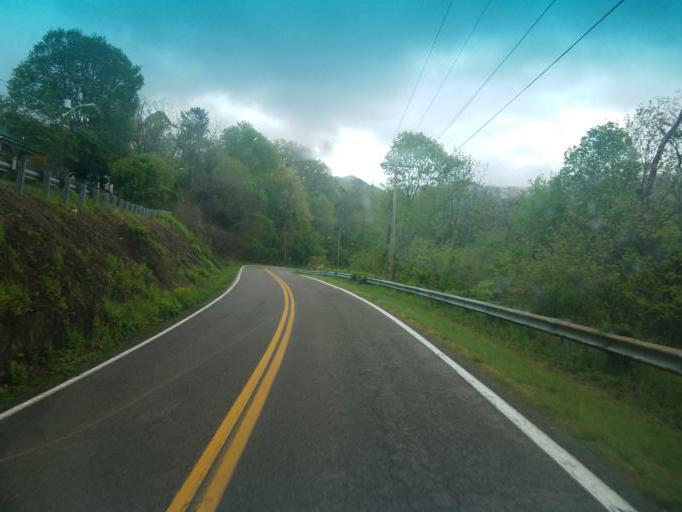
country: US
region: Virginia
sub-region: Washington County
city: Emory
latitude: 36.6370
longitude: -81.7874
